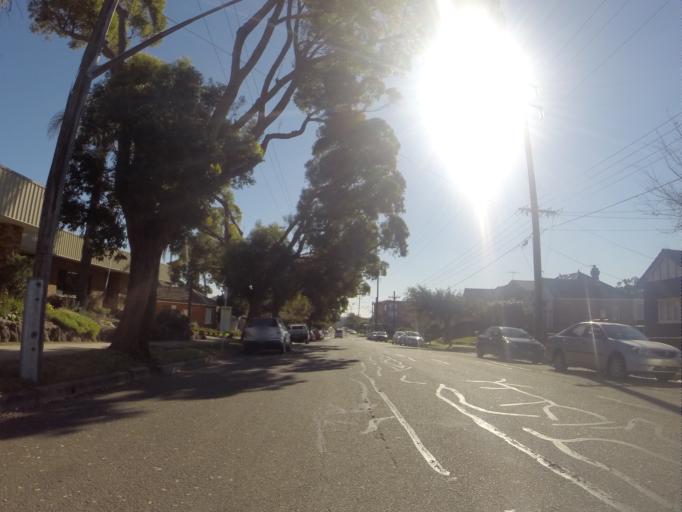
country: AU
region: New South Wales
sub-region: Hurstville
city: Earlwood
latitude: -33.9609
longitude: 151.0951
